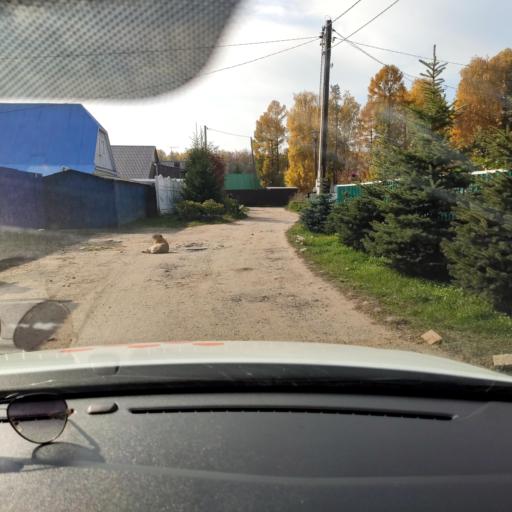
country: RU
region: Tatarstan
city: Stolbishchi
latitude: 55.6796
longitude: 49.1129
